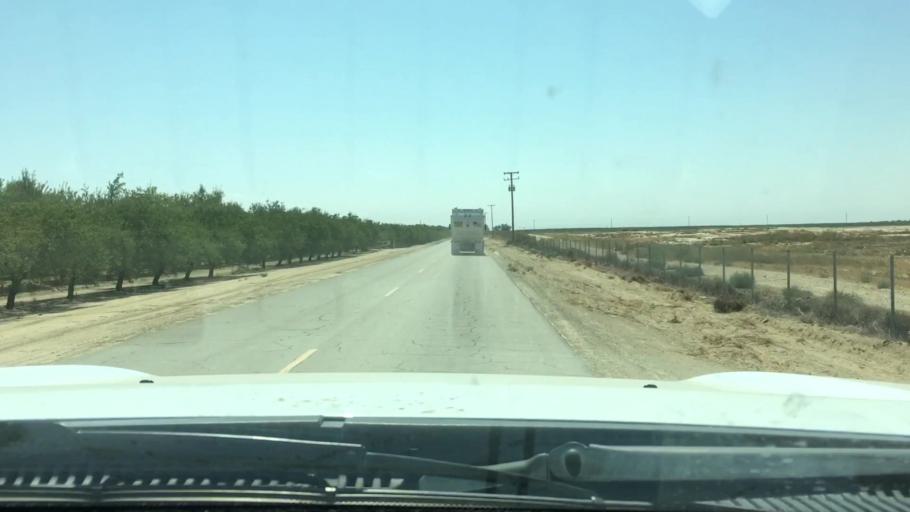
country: US
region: California
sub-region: Kern County
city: Wasco
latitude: 35.5125
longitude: -119.4033
